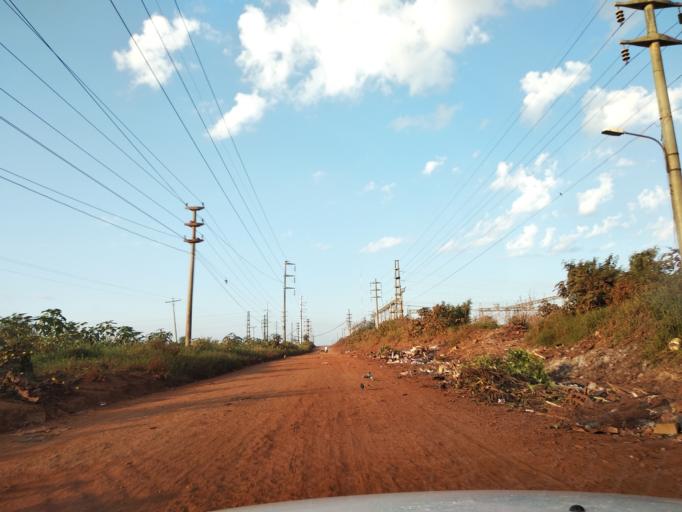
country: AR
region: Misiones
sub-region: Departamento de Capital
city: Posadas
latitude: -27.4400
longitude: -55.9159
